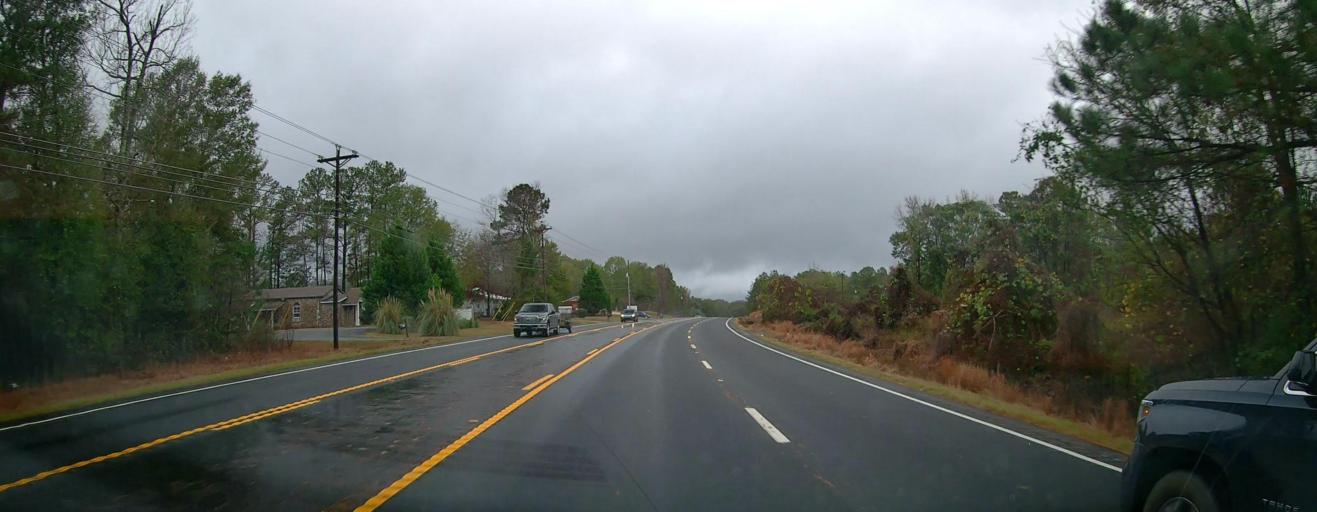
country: US
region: Georgia
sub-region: Clarke County
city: Country Club Estates
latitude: 34.0059
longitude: -83.3867
